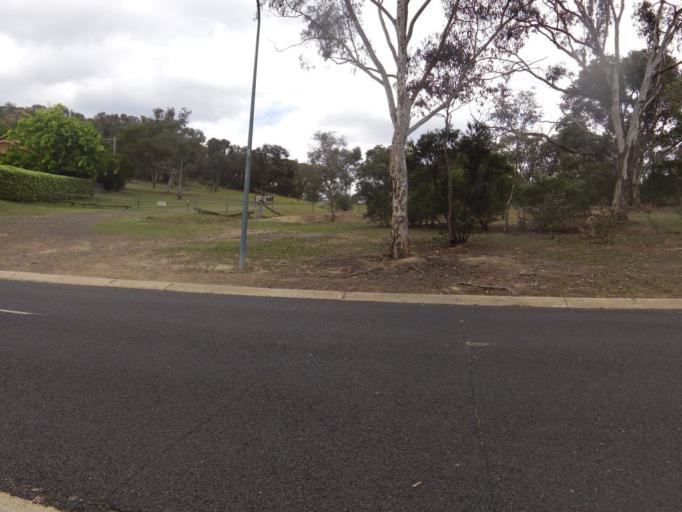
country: AU
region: Australian Capital Territory
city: Macarthur
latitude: -35.4014
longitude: 149.1299
